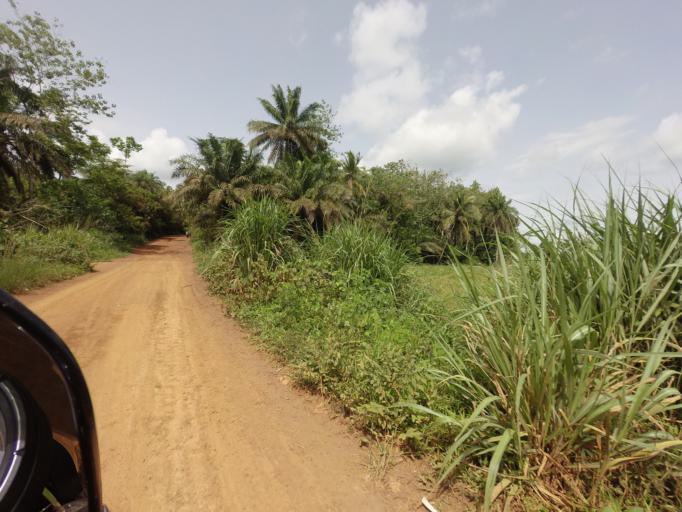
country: SL
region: Northern Province
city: Kambia
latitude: 9.1035
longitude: -12.9688
